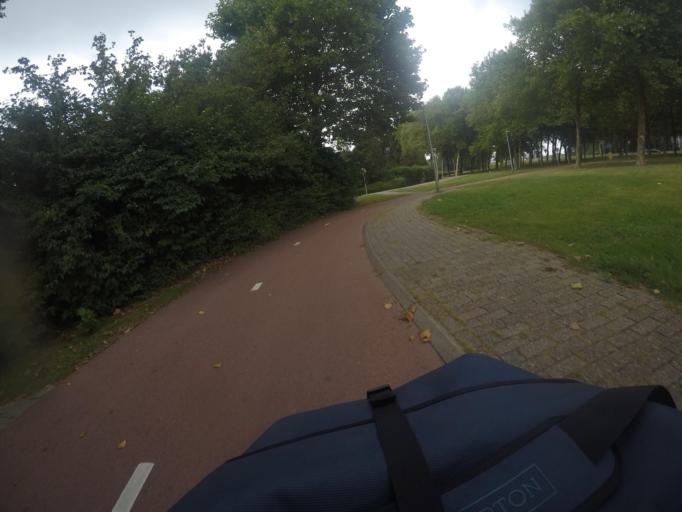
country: NL
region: Flevoland
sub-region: Gemeente Almere
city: Almere Stad
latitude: 52.3494
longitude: 5.2165
